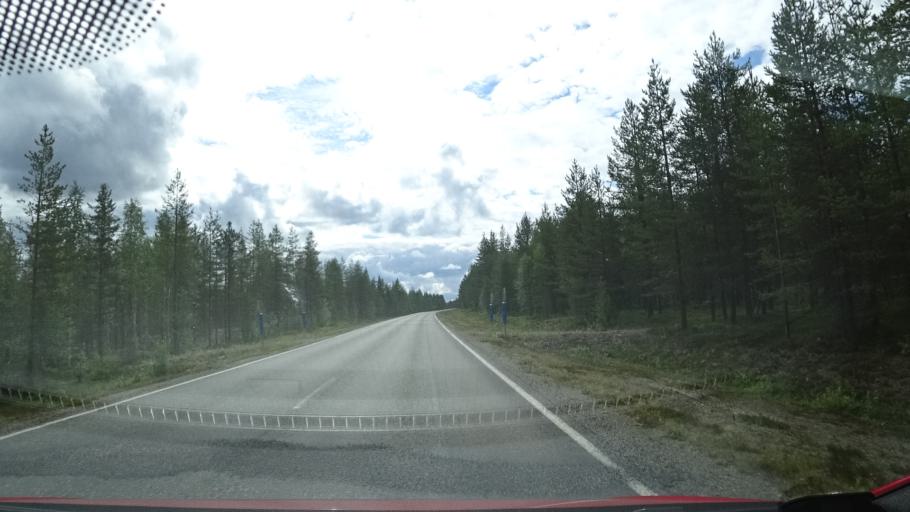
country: FI
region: Lapland
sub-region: Tunturi-Lappi
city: Kittilae
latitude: 67.5192
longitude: 24.9057
